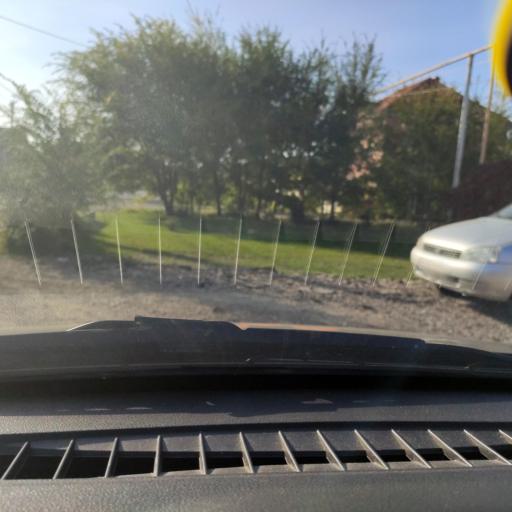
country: RU
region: Samara
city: Tol'yatti
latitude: 53.5446
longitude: 49.3760
